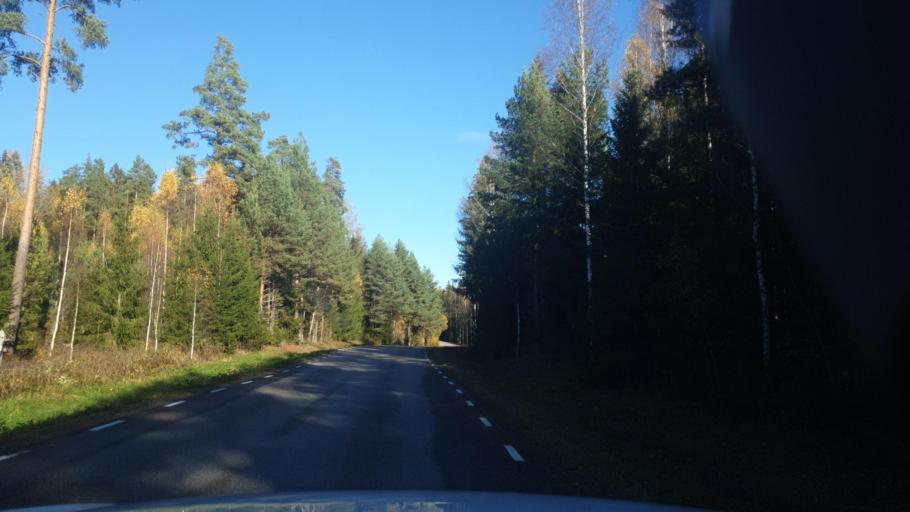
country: SE
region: Vaermland
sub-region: Arvika Kommun
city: Arvika
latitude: 59.6109
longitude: 12.7784
